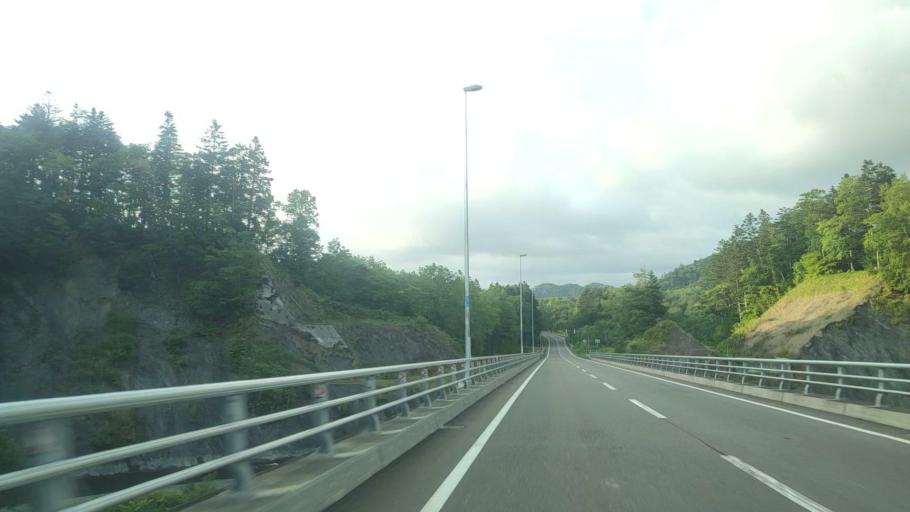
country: JP
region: Hokkaido
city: Bibai
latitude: 43.1095
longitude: 142.0986
